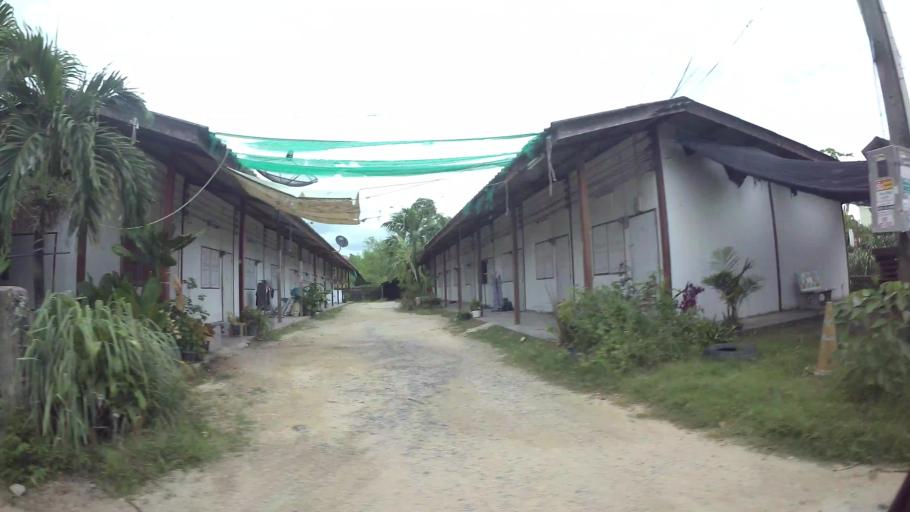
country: TH
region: Chon Buri
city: Si Racha
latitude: 13.1602
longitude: 100.9698
